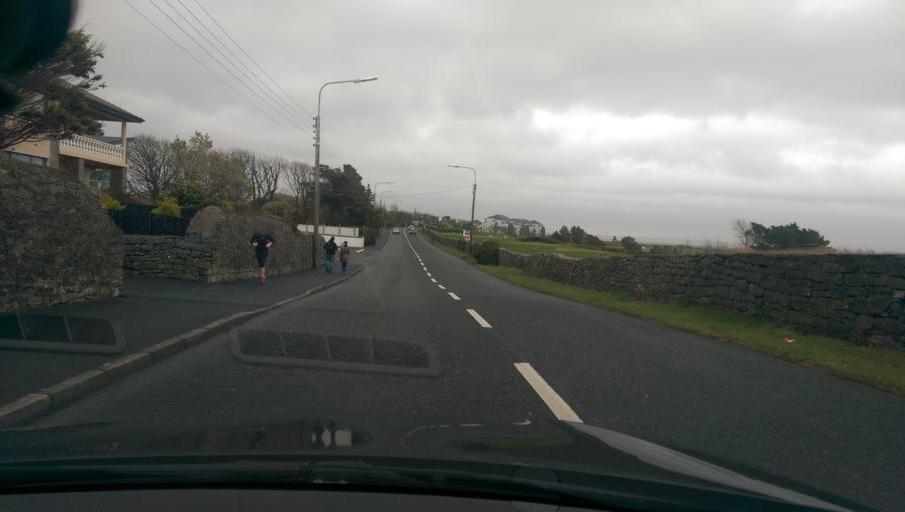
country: IE
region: Connaught
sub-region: County Galway
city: Bearna
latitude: 53.2583
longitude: -9.1004
